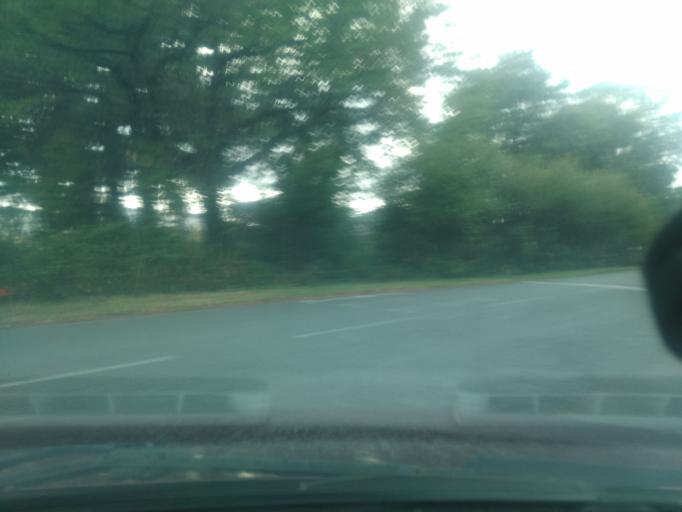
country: FR
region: Pays de la Loire
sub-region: Departement de la Vendee
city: Dompierre-sur-Yon
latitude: 46.6961
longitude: -1.3752
